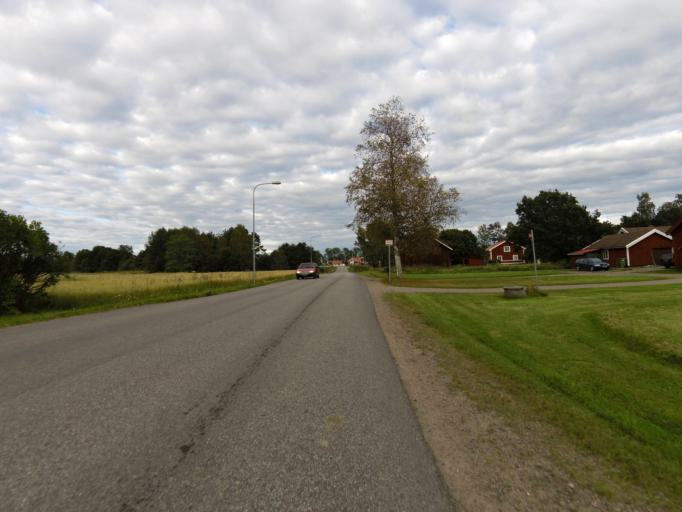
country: SE
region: Gaevleborg
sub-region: Gavle Kommun
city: Valbo
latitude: 60.6499
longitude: 16.9971
